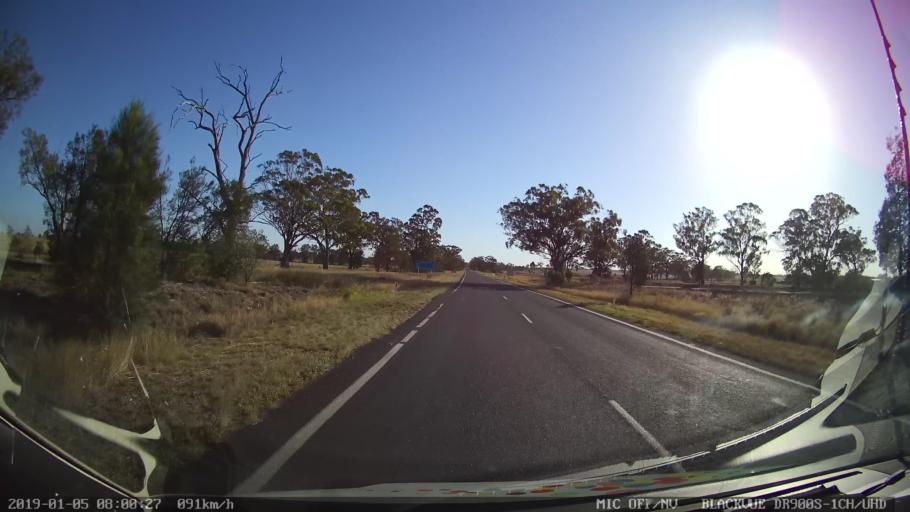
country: AU
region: New South Wales
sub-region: Gilgandra
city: Gilgandra
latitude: -31.6932
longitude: 148.6887
